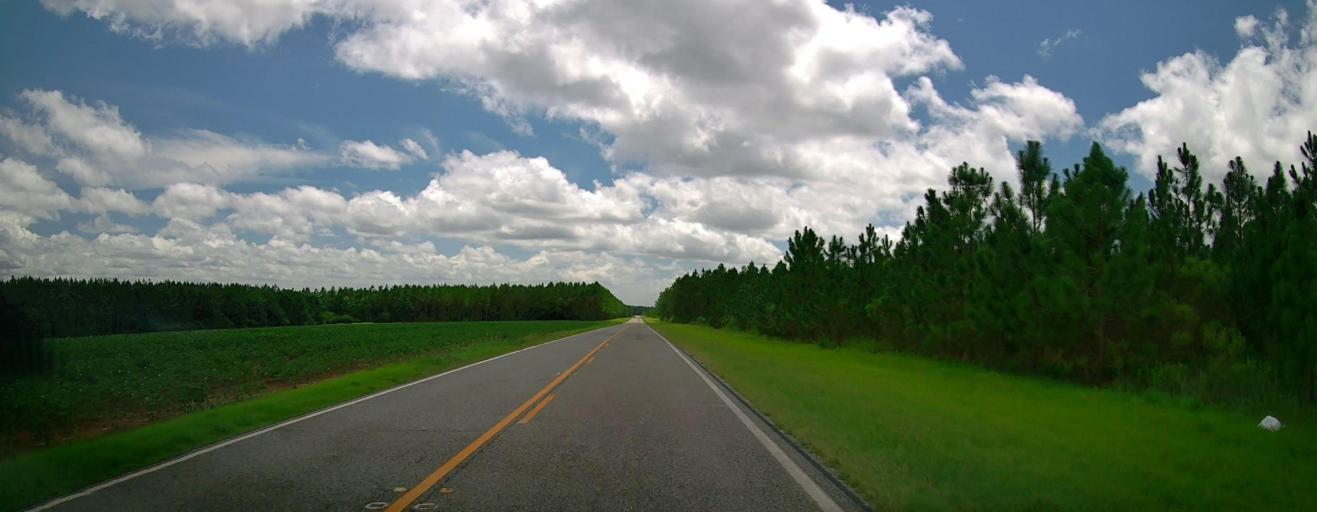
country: US
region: Georgia
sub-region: Wilcox County
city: Rochelle
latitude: 31.8746
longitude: -83.5584
